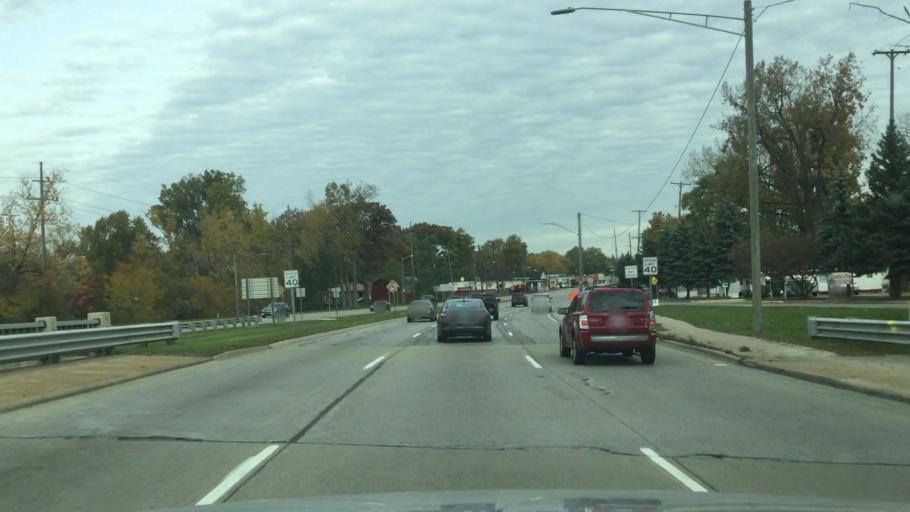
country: US
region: Michigan
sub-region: Oakland County
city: Sylvan Lake
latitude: 42.6224
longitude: -83.3246
